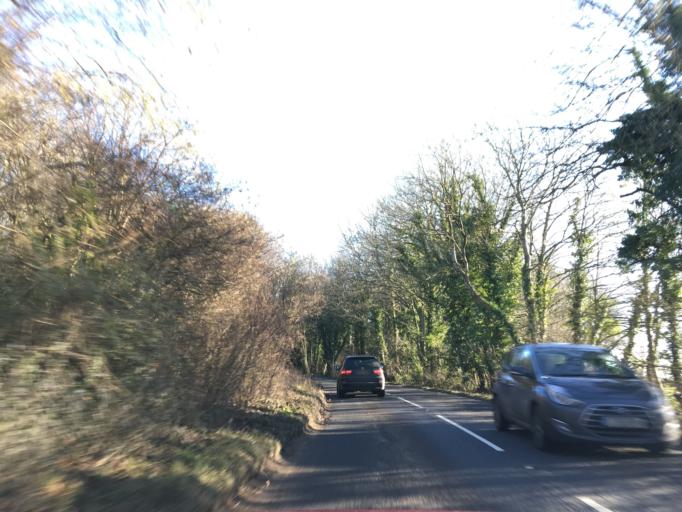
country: GB
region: England
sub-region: Wiltshire
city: Biddestone
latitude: 51.4932
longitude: -2.2084
